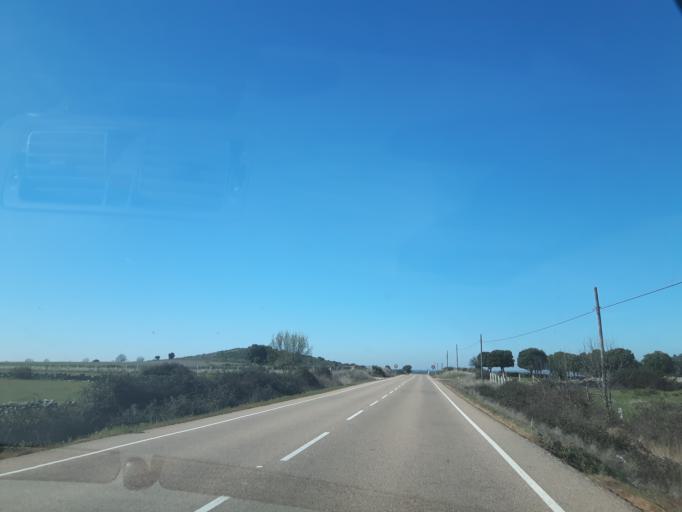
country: ES
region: Castille and Leon
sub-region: Provincia de Salamanca
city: Guadramiro
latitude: 41.0035
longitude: -6.5082
